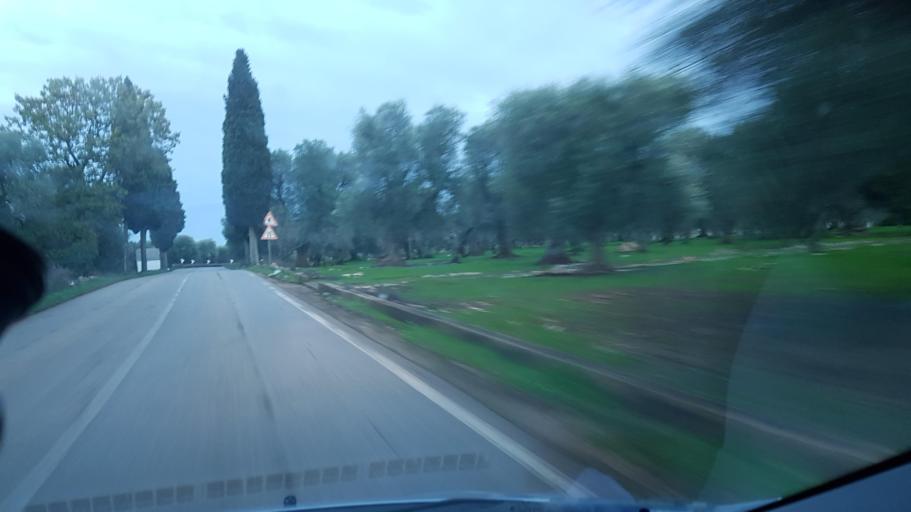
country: IT
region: Apulia
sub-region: Provincia di Brindisi
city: Ceglie Messapica
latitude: 40.6433
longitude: 17.5702
